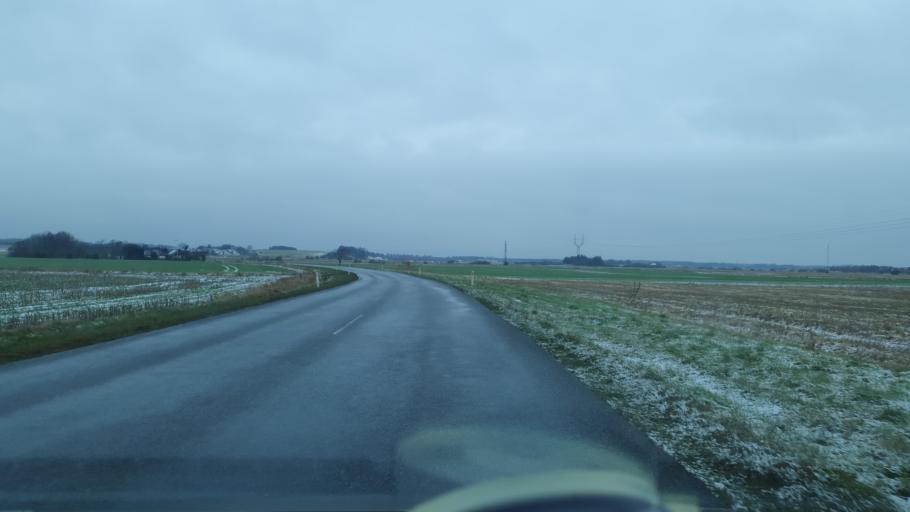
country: DK
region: North Denmark
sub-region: Jammerbugt Kommune
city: Brovst
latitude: 57.1151
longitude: 9.5005
